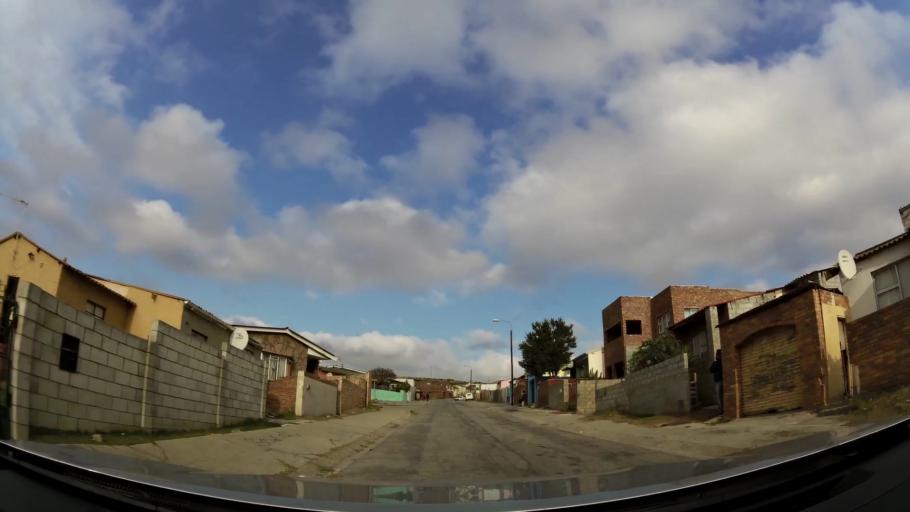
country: ZA
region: Eastern Cape
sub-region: Nelson Mandela Bay Metropolitan Municipality
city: Port Elizabeth
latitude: -33.9151
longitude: 25.5453
